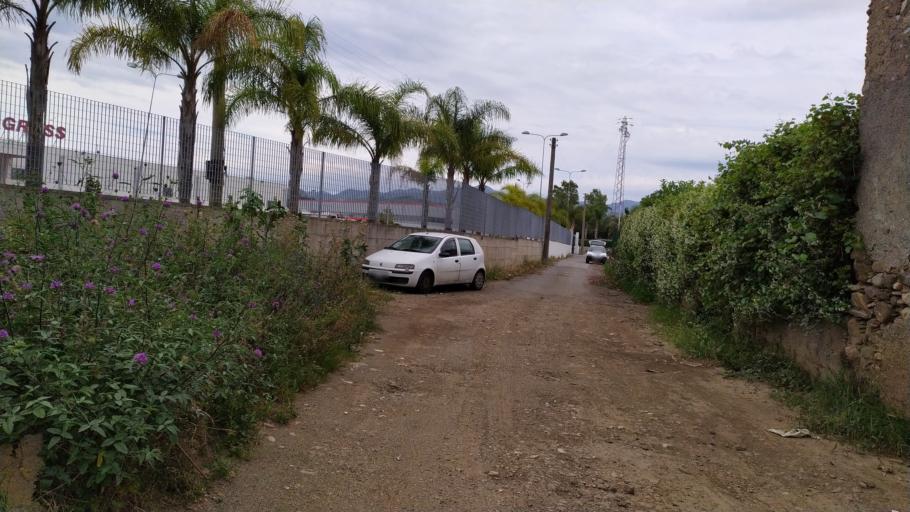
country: IT
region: Sicily
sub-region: Messina
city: San Filippo del Mela
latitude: 38.1868
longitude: 15.2647
